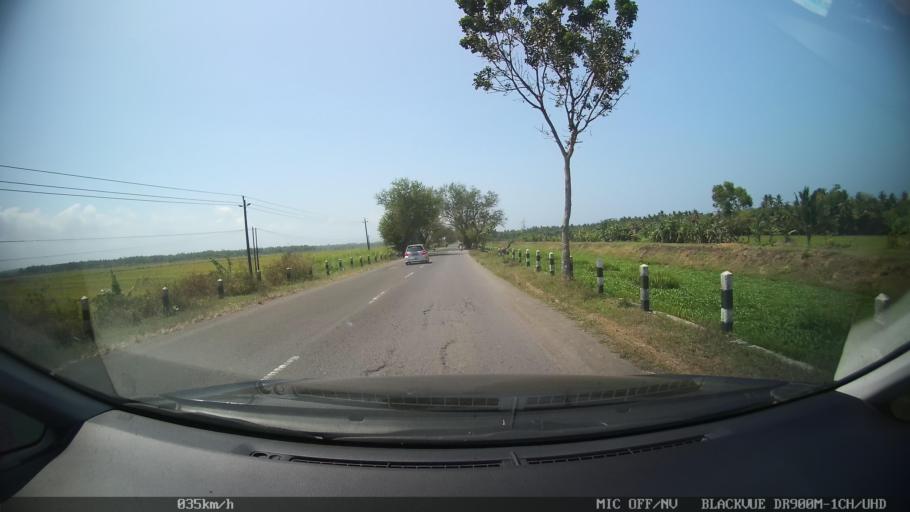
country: ID
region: Daerah Istimewa Yogyakarta
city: Srandakan
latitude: -7.9450
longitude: 110.1739
